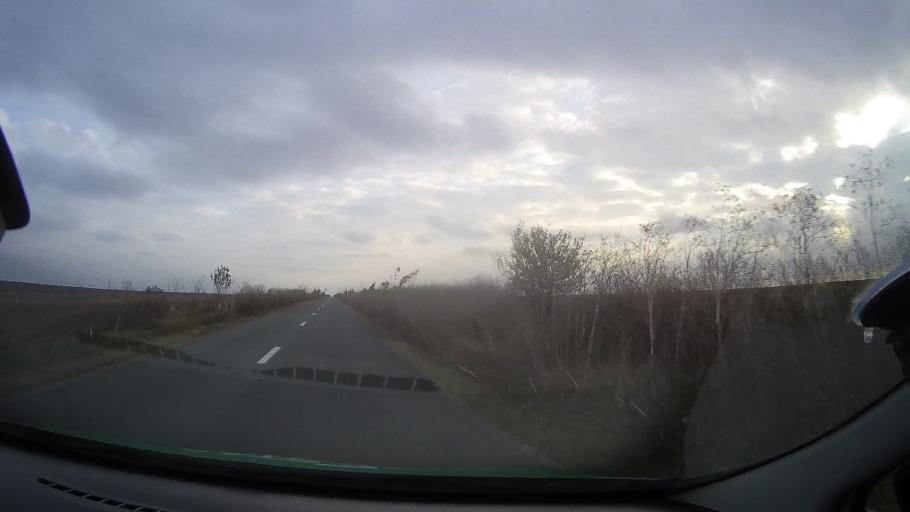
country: RO
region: Constanta
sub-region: Comuna Pestera
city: Pestera
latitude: 44.1441
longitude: 28.1160
